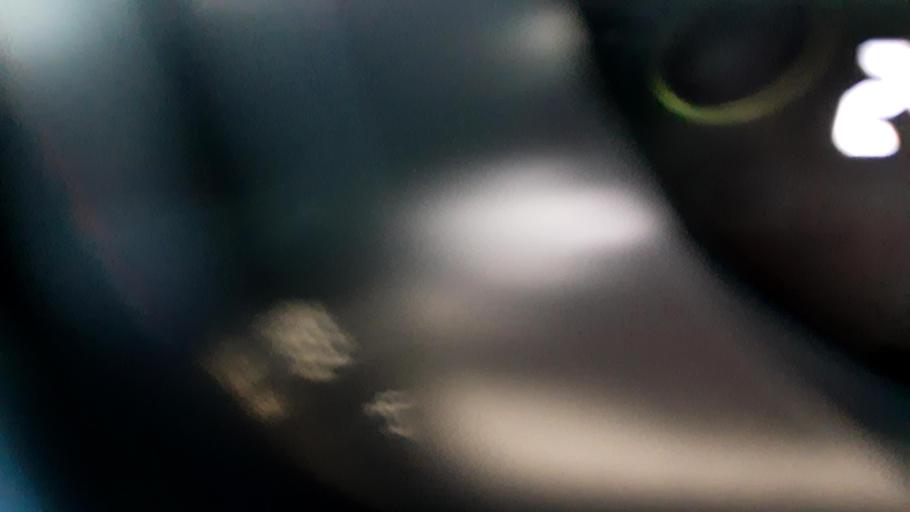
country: RU
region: Nizjnij Novgorod
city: Bor
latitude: 56.3589
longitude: 44.0729
